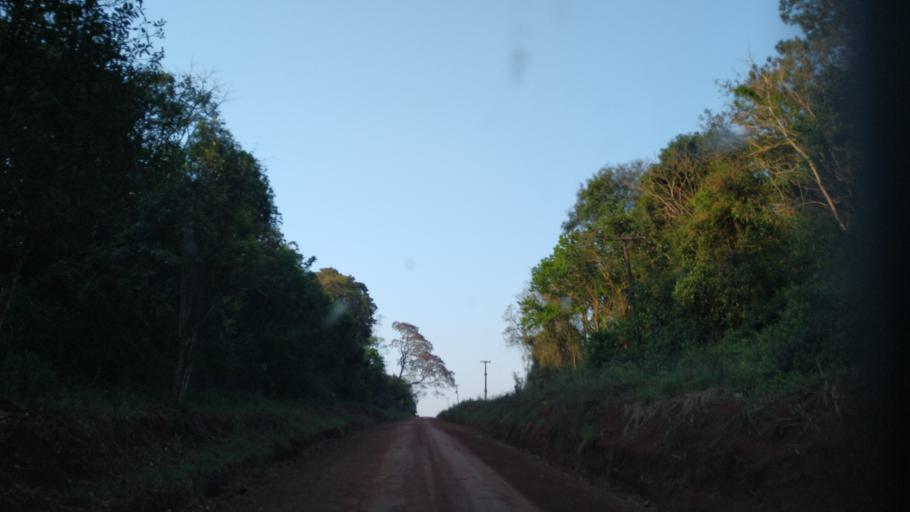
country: AR
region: Misiones
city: Jardin America
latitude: -27.0828
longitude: -55.2746
